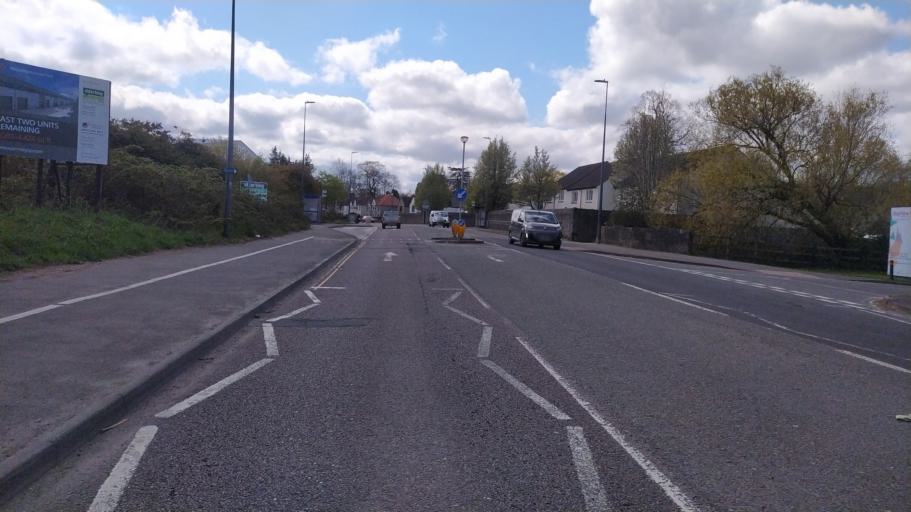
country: GB
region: England
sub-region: South Gloucestershire
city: Siston
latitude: 51.4571
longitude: -2.4763
